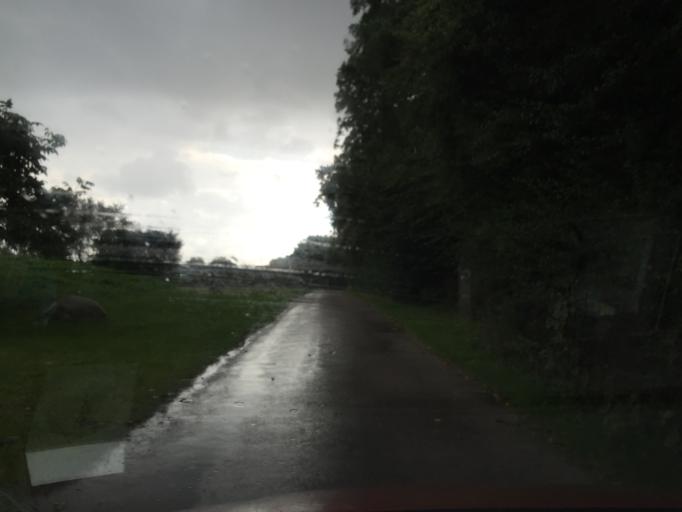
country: DK
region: South Denmark
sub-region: Sonderborg Kommune
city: Dybbol
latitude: 54.9567
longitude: 9.7369
